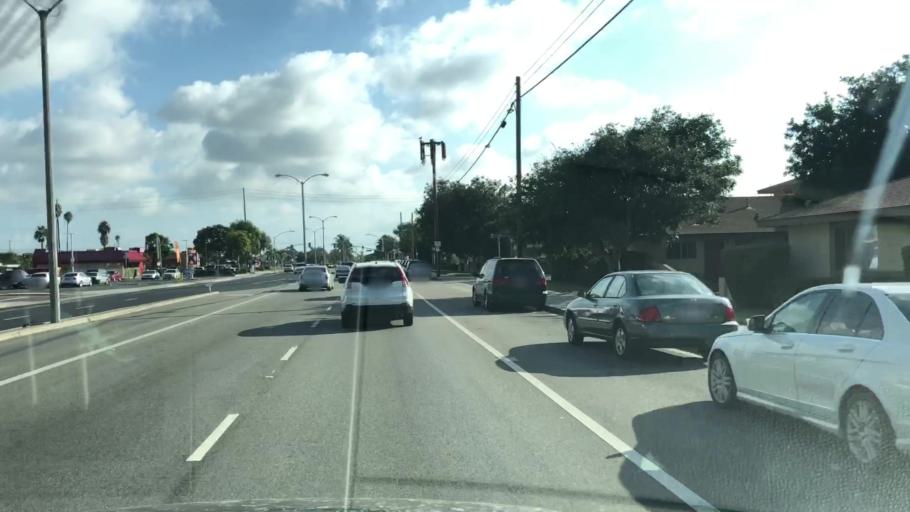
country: US
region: California
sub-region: Ventura County
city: Oxnard
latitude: 34.2215
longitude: -119.1946
